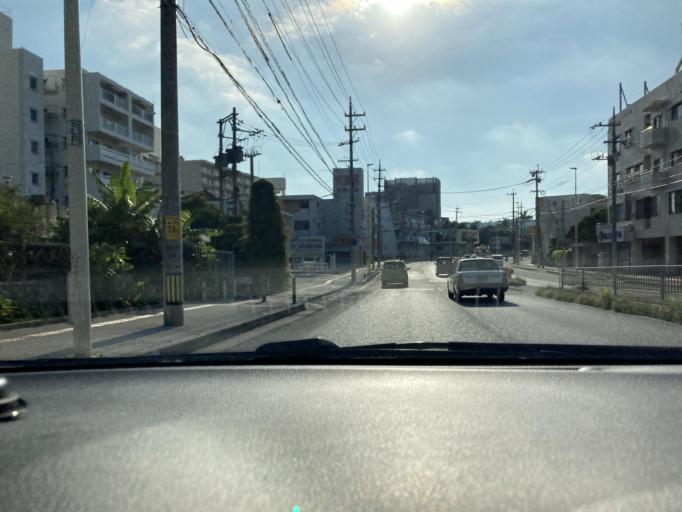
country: JP
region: Okinawa
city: Naha-shi
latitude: 26.2362
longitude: 127.6984
